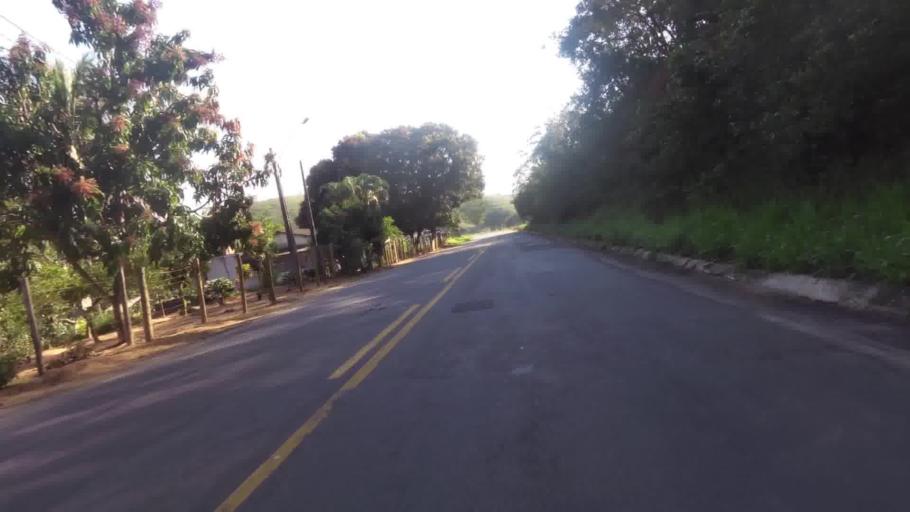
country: BR
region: Espirito Santo
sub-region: Alfredo Chaves
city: Alfredo Chaves
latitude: -20.6846
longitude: -40.7066
